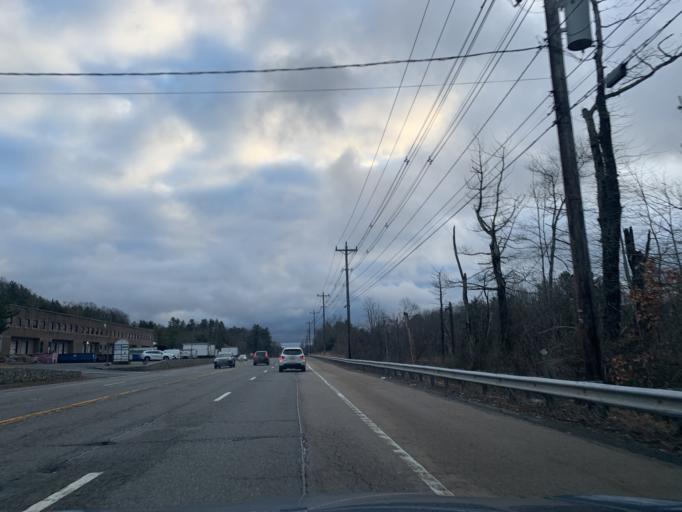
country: US
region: Massachusetts
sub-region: Norfolk County
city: Wrentham
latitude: 42.0601
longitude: -71.2963
